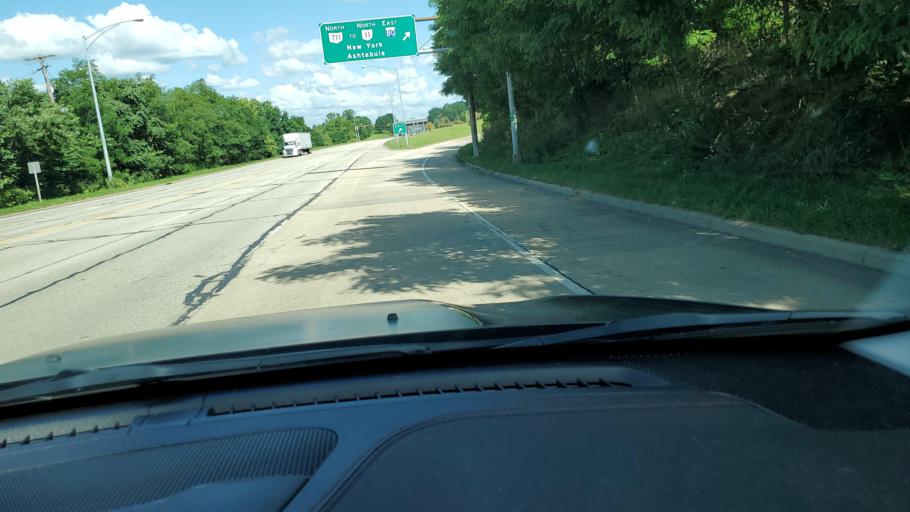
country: US
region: Ohio
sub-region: Mahoning County
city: Youngstown
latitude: 41.1201
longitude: -80.6744
